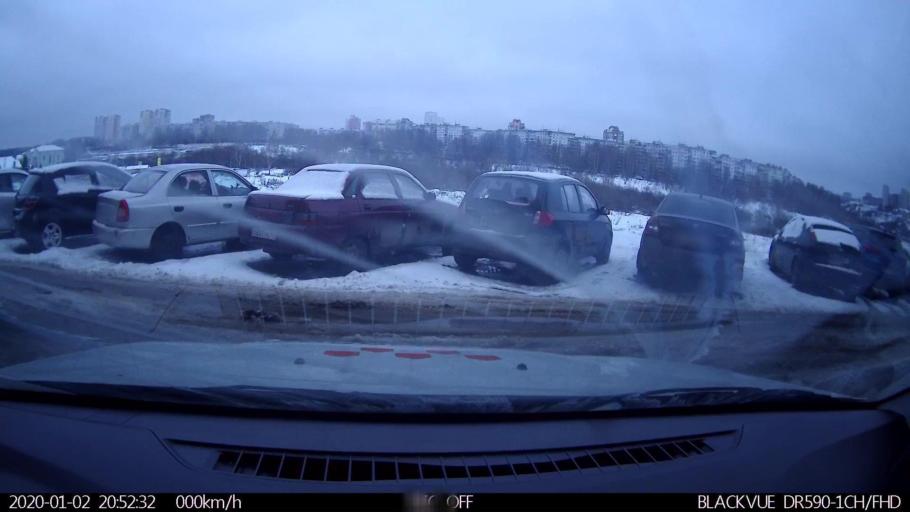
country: RU
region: Nizjnij Novgorod
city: Afonino
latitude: 56.2758
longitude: 44.0470
